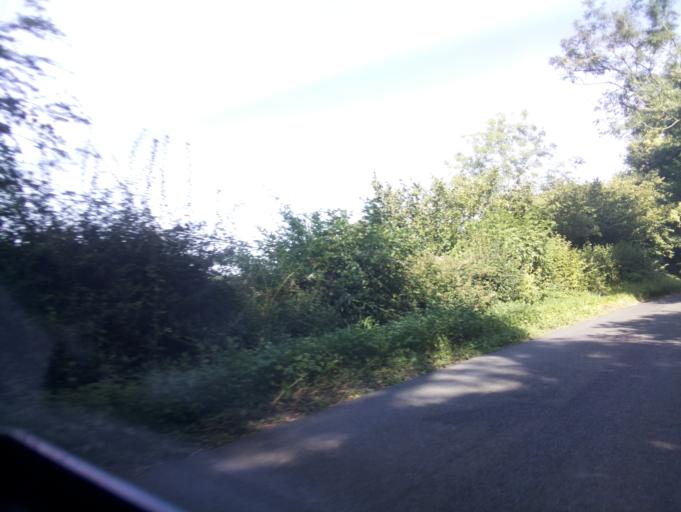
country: GB
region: England
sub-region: Gloucestershire
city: Dursley
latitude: 51.6771
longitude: -2.2991
